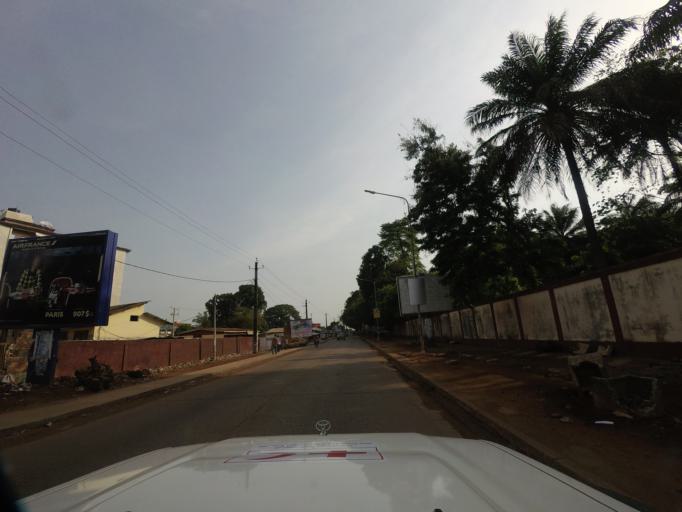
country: GN
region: Conakry
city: Camayenne
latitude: 9.5304
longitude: -13.6874
